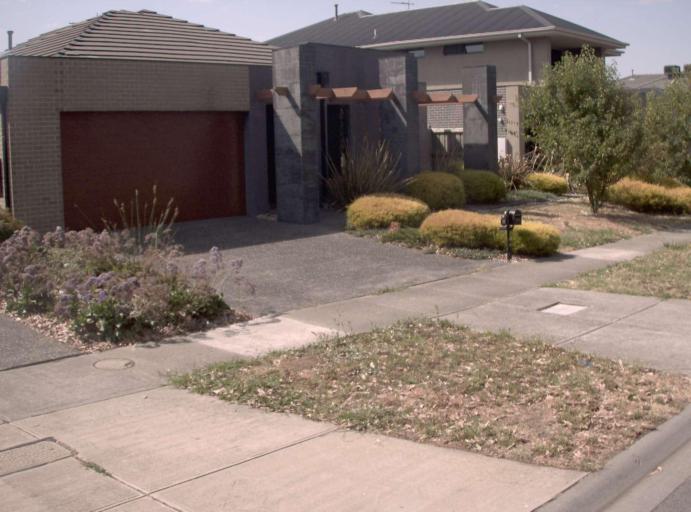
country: AU
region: Victoria
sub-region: Kingston
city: Waterways
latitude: -38.0113
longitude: 145.1323
